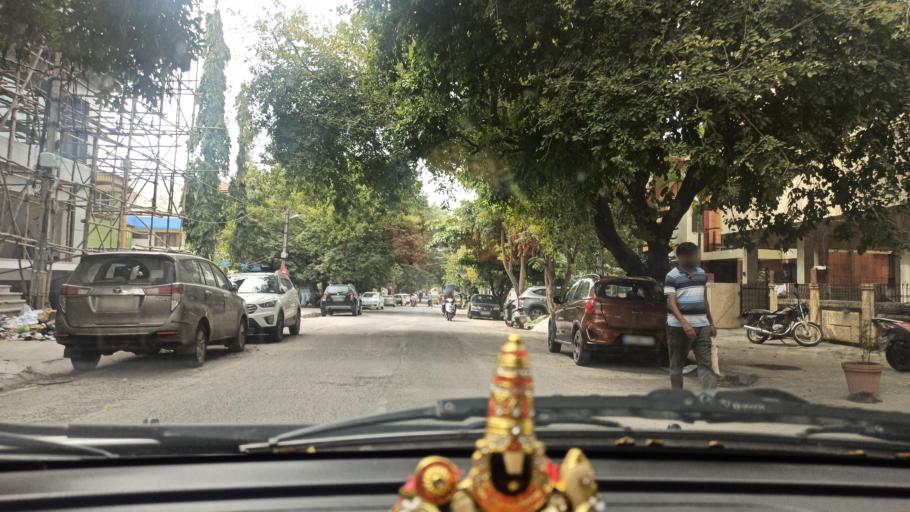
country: IN
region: Karnataka
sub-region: Bangalore Urban
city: Bangalore
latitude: 13.0183
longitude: 77.6485
